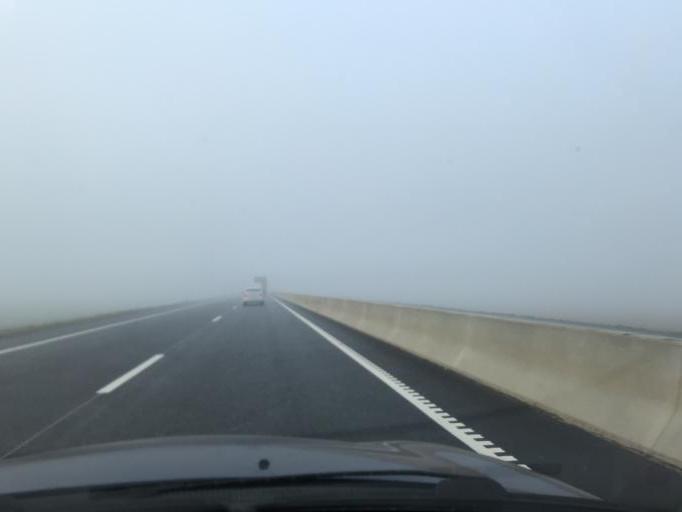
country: BY
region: Minsk
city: Valozhyn
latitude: 54.0572
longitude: 26.4937
